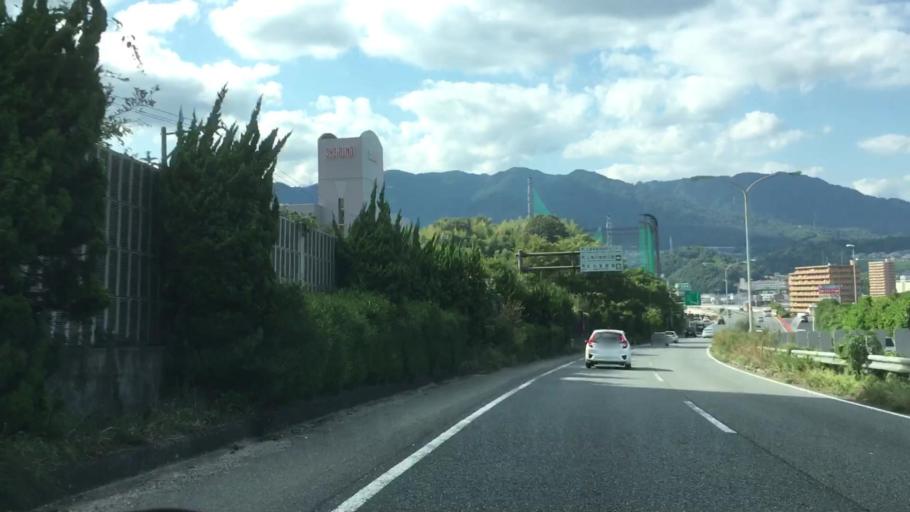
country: JP
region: Hiroshima
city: Hatsukaichi
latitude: 34.3769
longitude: 132.3675
